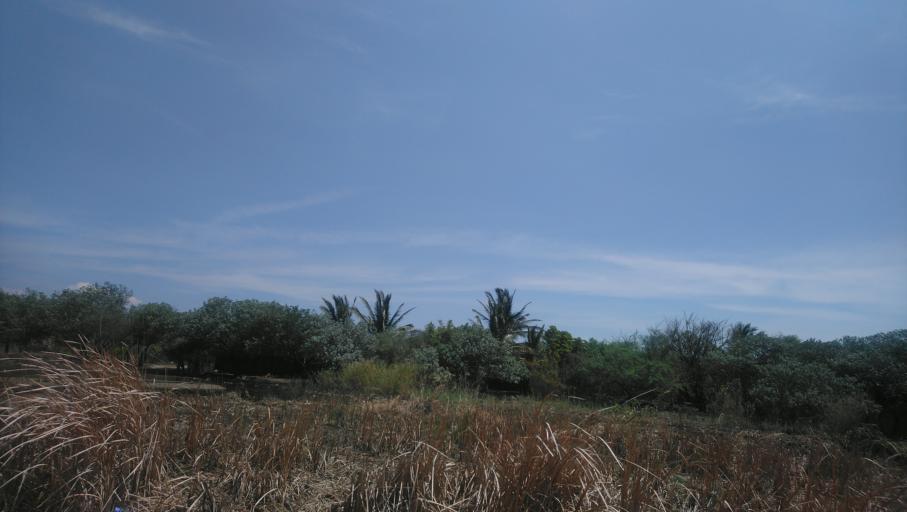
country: MX
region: Oaxaca
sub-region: Salina Cruz
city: Salina Cruz
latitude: 16.1917
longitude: -95.1207
